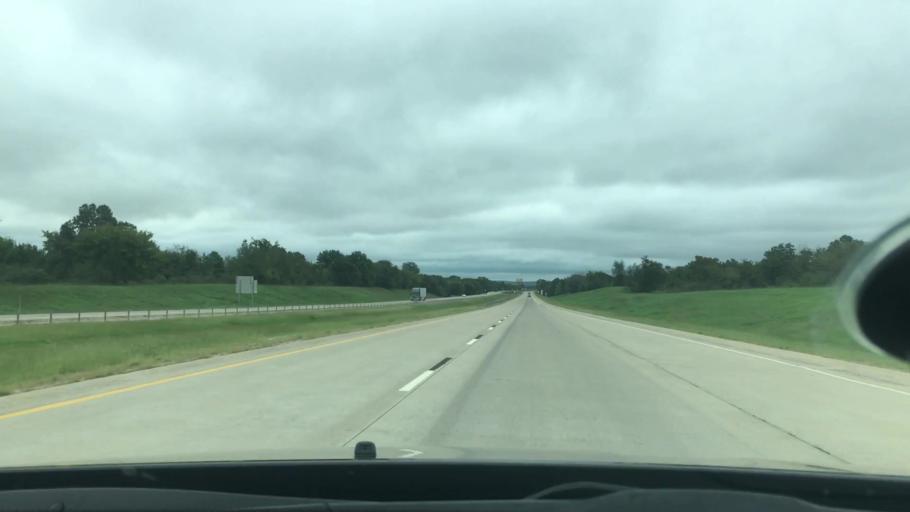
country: US
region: Oklahoma
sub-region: Muskogee County
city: Warner
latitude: 35.4843
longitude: -95.1991
